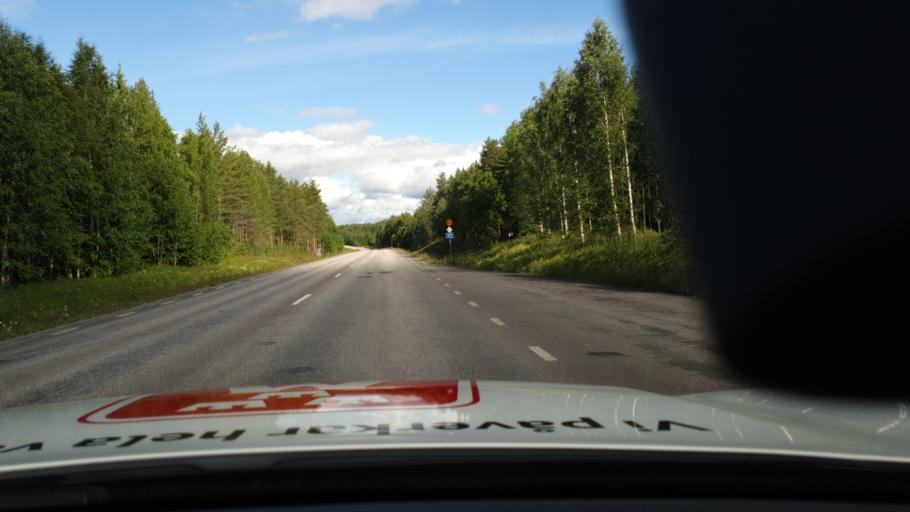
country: SE
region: Norrbotten
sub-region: Bodens Kommun
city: Boden
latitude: 65.8900
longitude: 21.3892
